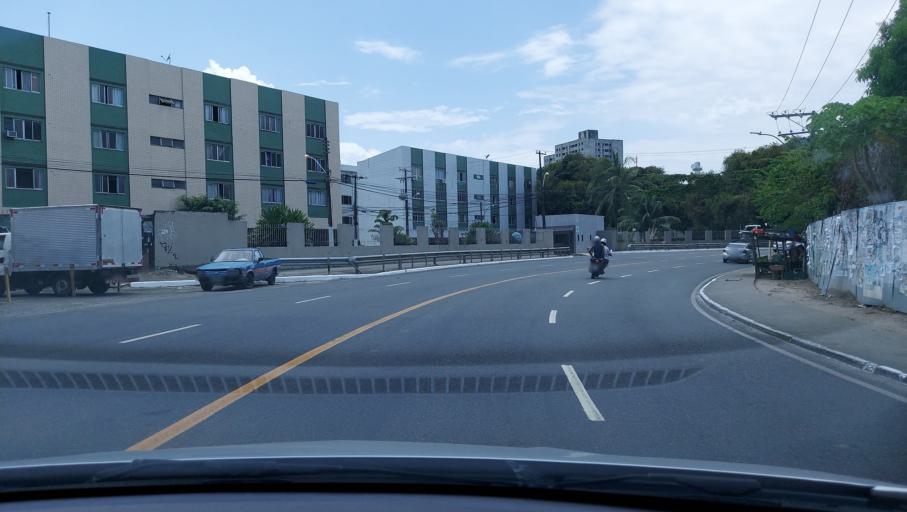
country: BR
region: Bahia
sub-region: Salvador
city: Salvador
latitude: -12.9613
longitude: -38.4707
